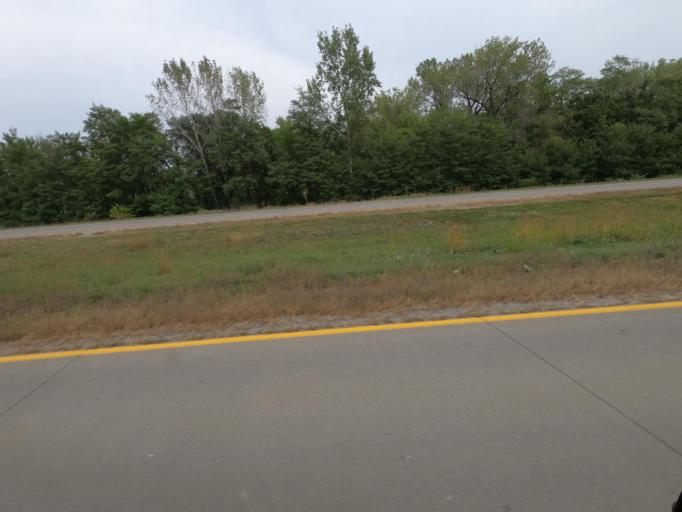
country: US
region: Iowa
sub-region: Marion County
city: Pella
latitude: 41.4010
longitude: -92.9371
